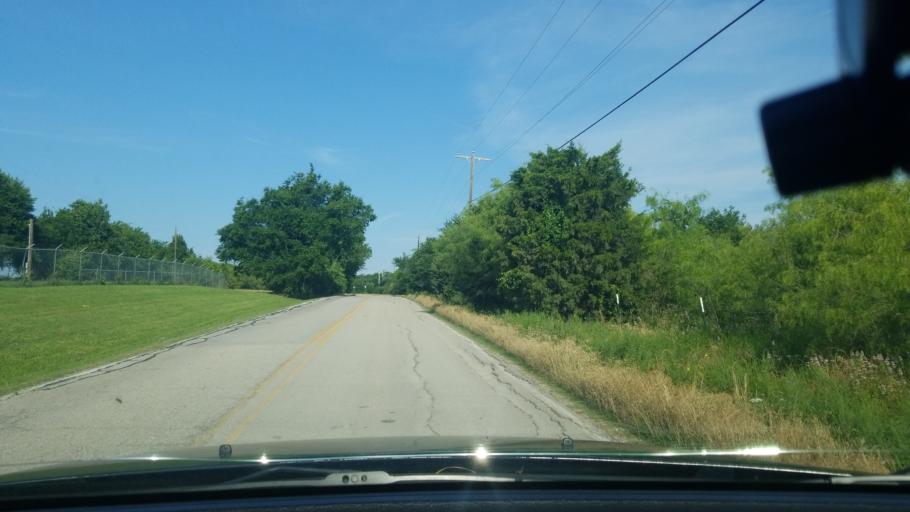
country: US
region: Texas
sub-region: Dallas County
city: Sunnyvale
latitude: 32.7729
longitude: -96.5578
